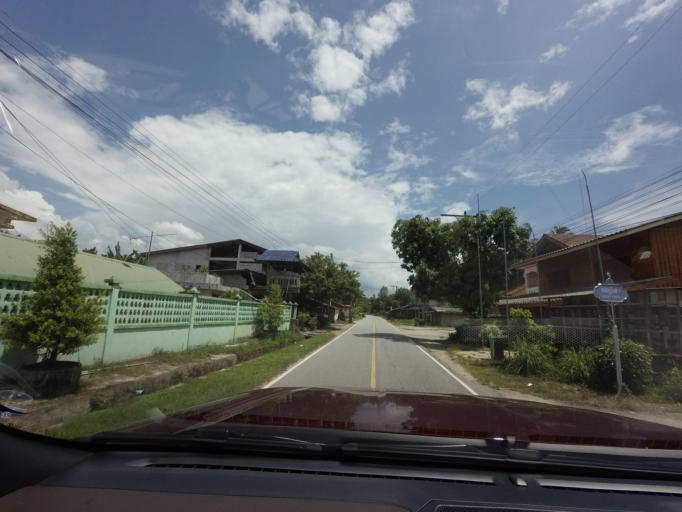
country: TH
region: Narathiwat
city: Chanae
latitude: 6.0881
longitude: 101.6926
